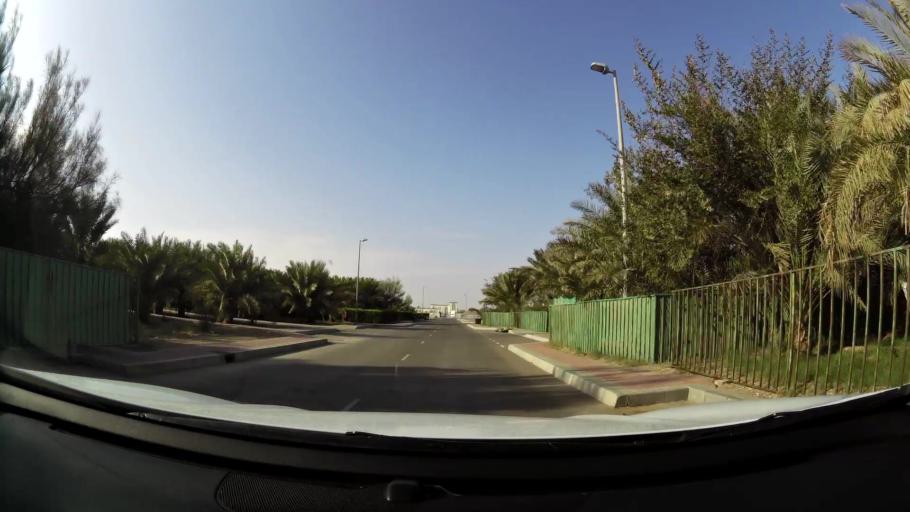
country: AE
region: Abu Dhabi
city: Al Ain
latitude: 24.0627
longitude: 55.8490
